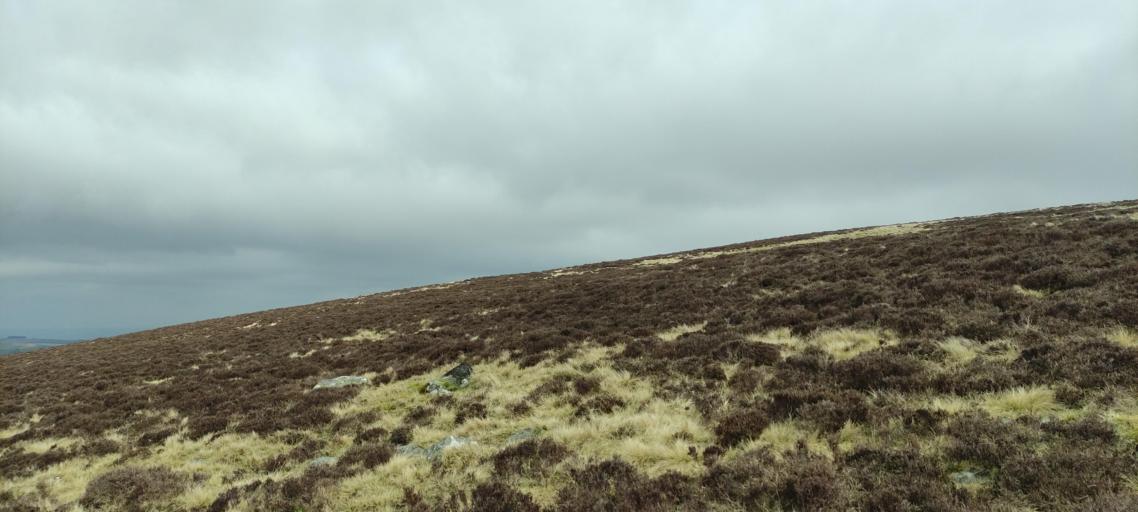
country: GB
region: England
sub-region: Cumbria
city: Keswick
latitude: 54.6955
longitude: -3.0755
